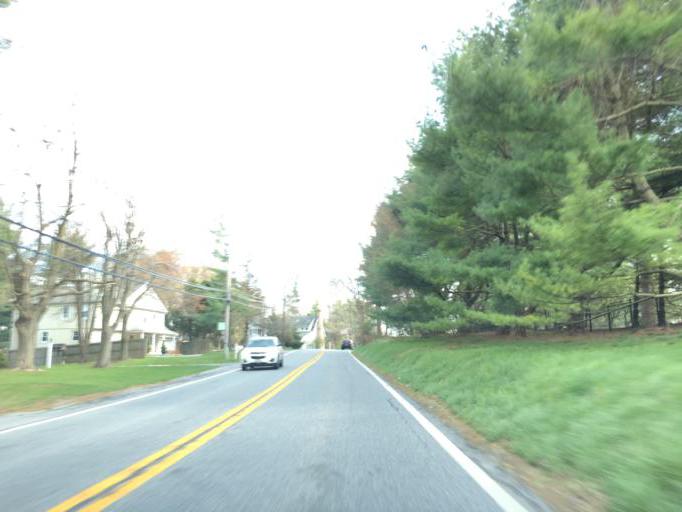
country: US
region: Maryland
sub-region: Baltimore County
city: Mays Chapel
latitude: 39.4614
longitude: -76.6991
